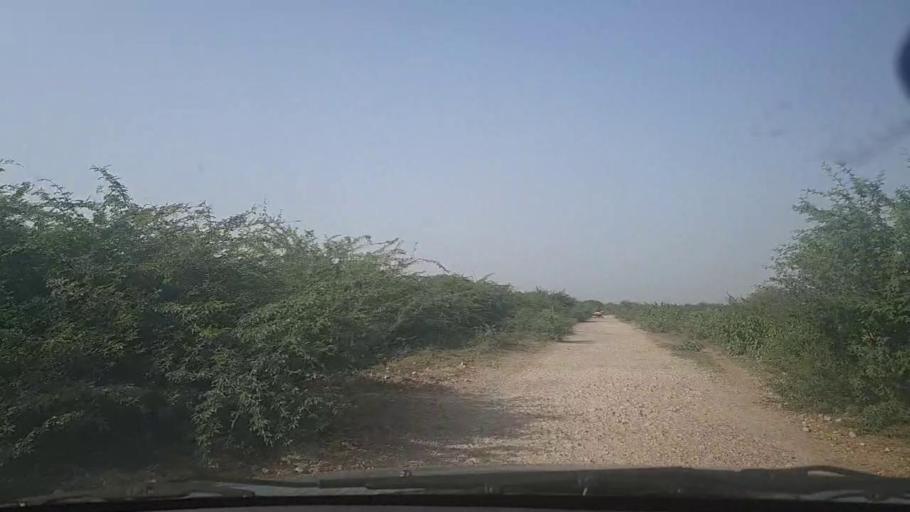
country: PK
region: Sindh
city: Keti Bandar
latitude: 24.2622
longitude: 67.5653
